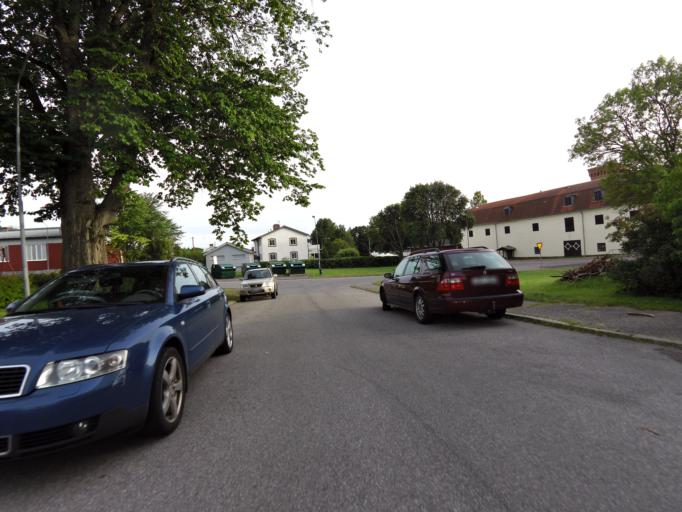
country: SE
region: Gaevleborg
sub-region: Gavle Kommun
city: Gavle
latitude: 60.6994
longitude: 17.1610
